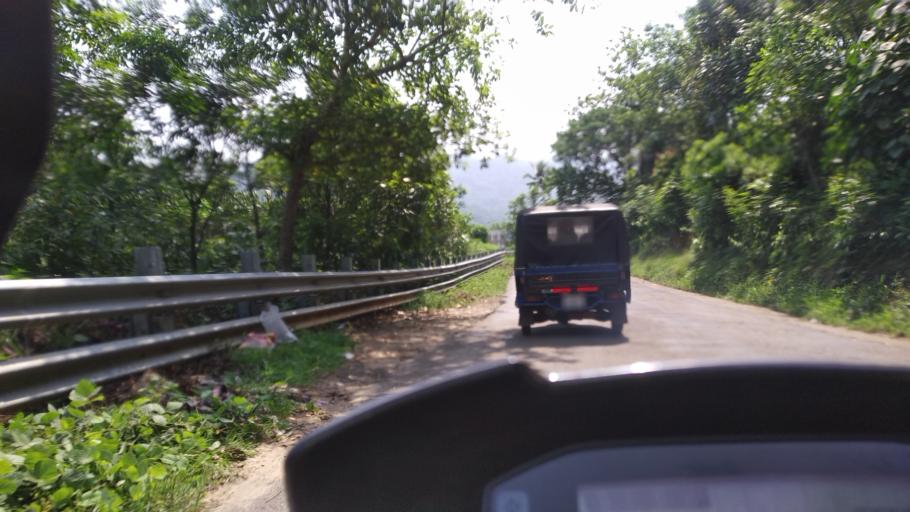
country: IN
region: Kerala
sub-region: Kottayam
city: Erattupetta
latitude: 9.6865
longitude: 76.8304
